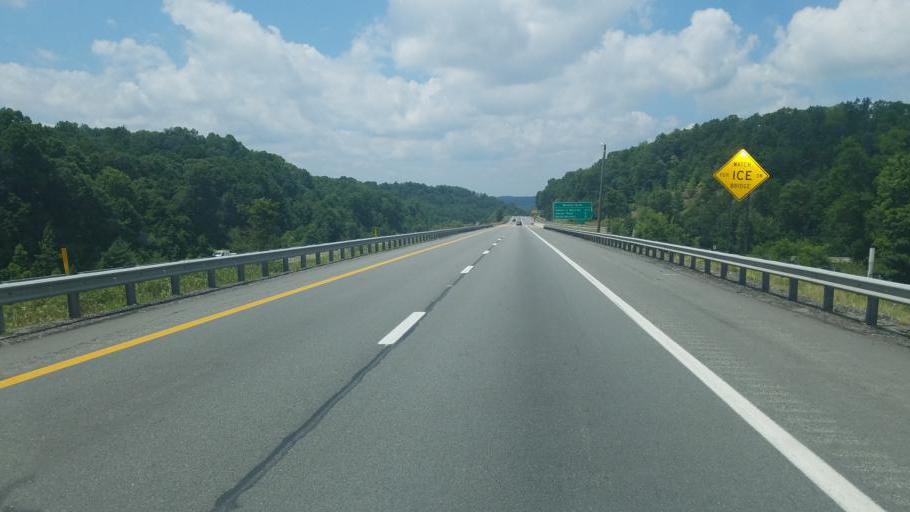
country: US
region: West Virginia
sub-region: Raleigh County
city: MacArthur
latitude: 37.7292
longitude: -81.1936
